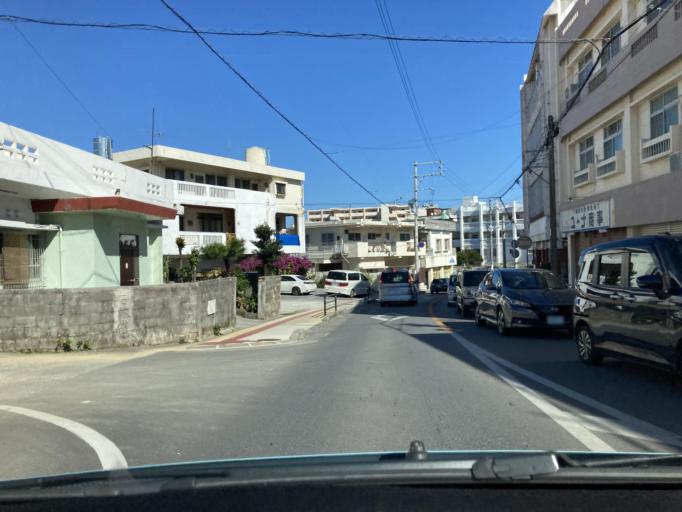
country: JP
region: Okinawa
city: Okinawa
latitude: 26.3314
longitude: 127.8081
